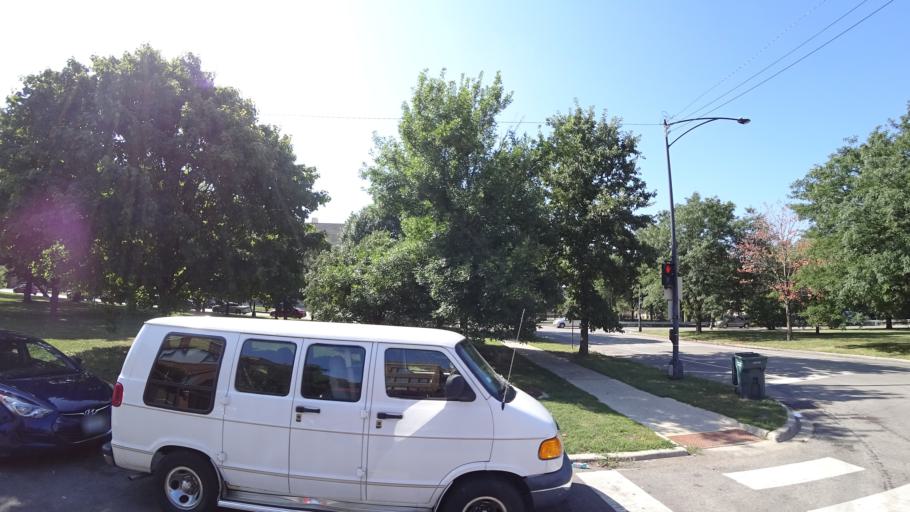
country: US
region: Illinois
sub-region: Cook County
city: Cicero
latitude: 41.8628
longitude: -87.7188
